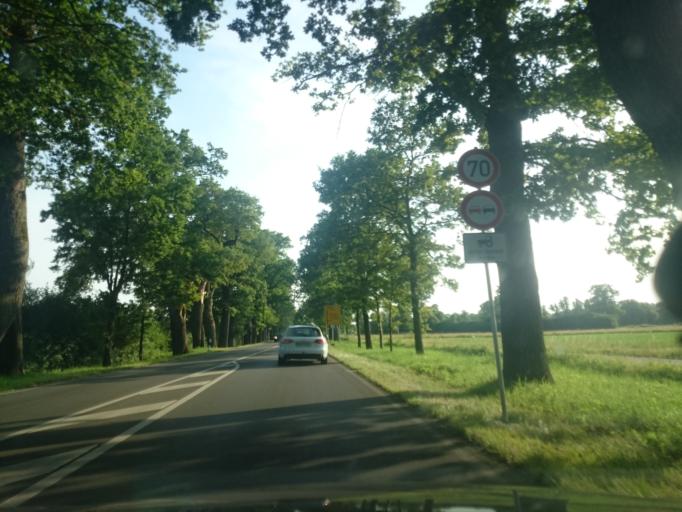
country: DE
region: Bavaria
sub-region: Upper Bavaria
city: Seefeld
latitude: 48.0433
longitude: 11.2128
